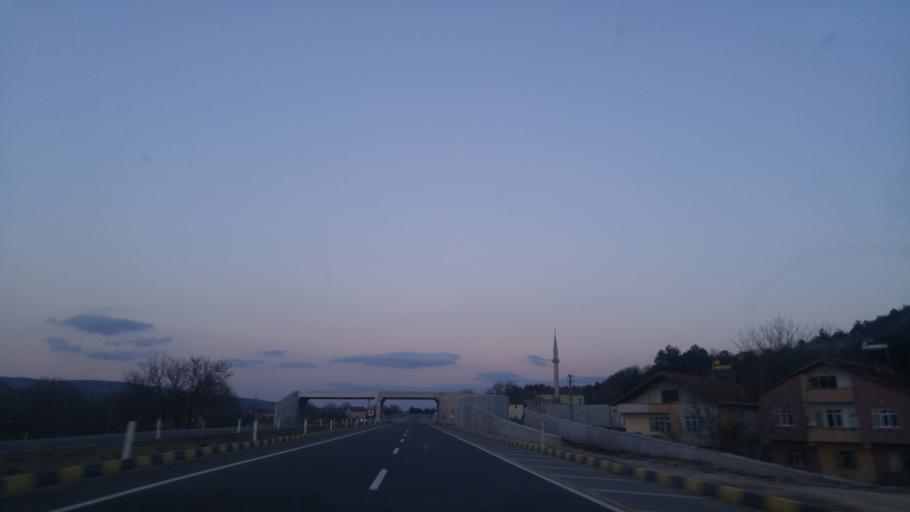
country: TR
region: Kastamonu
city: Igdir
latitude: 41.2287
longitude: 33.0947
